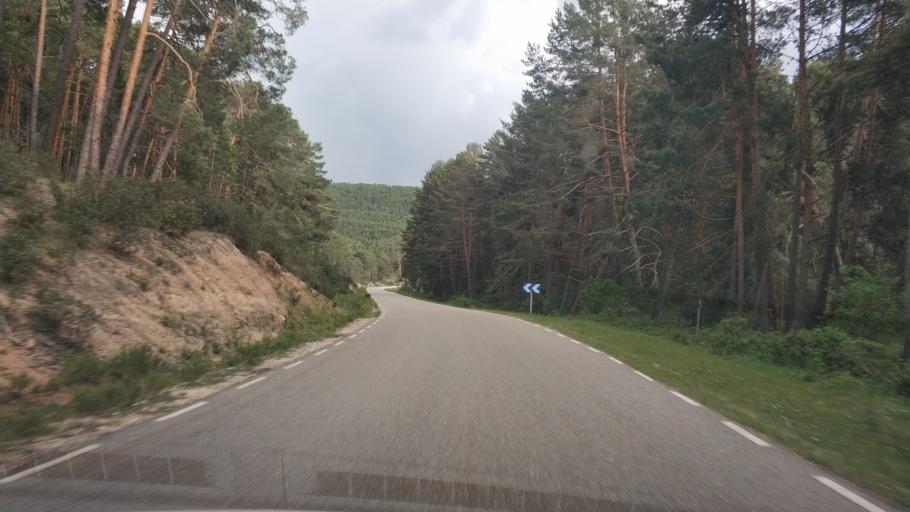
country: ES
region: Castille and Leon
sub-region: Provincia de Soria
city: San Leonardo de Yague
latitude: 41.8552
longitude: -3.0728
